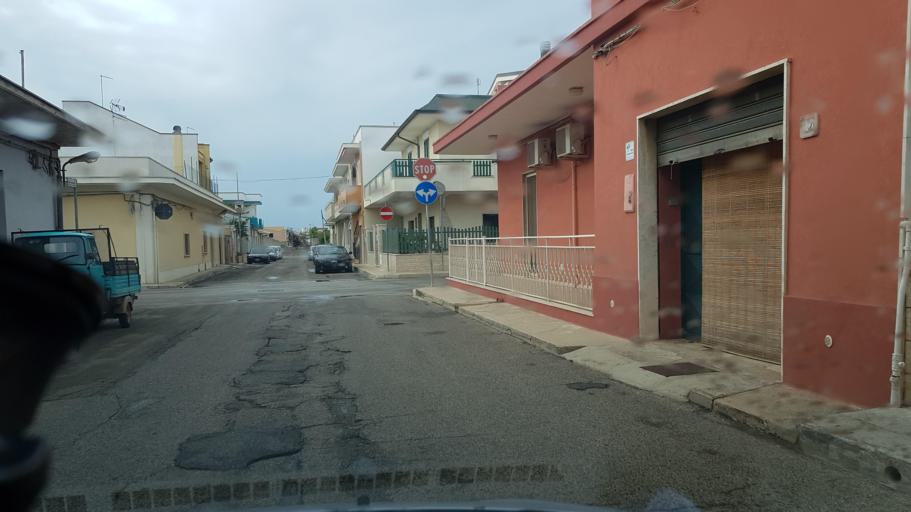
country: IT
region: Apulia
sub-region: Provincia di Brindisi
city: Torre Santa Susanna
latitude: 40.4668
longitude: 17.7346
